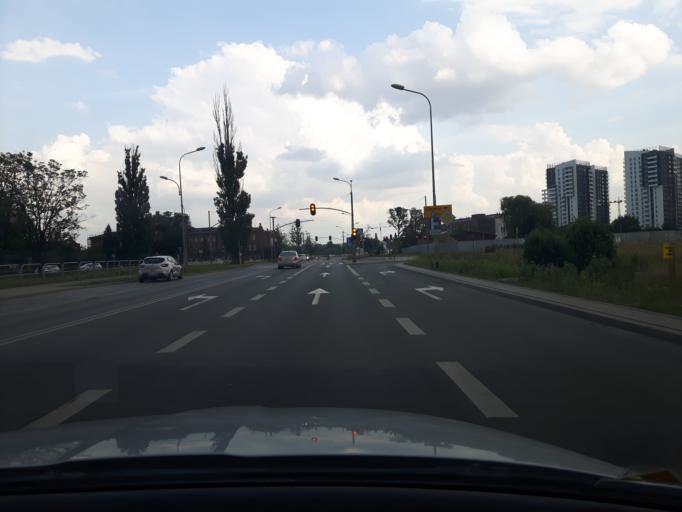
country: PL
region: Pomeranian Voivodeship
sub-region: Gdansk
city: Gdansk
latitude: 54.3630
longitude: 18.6499
